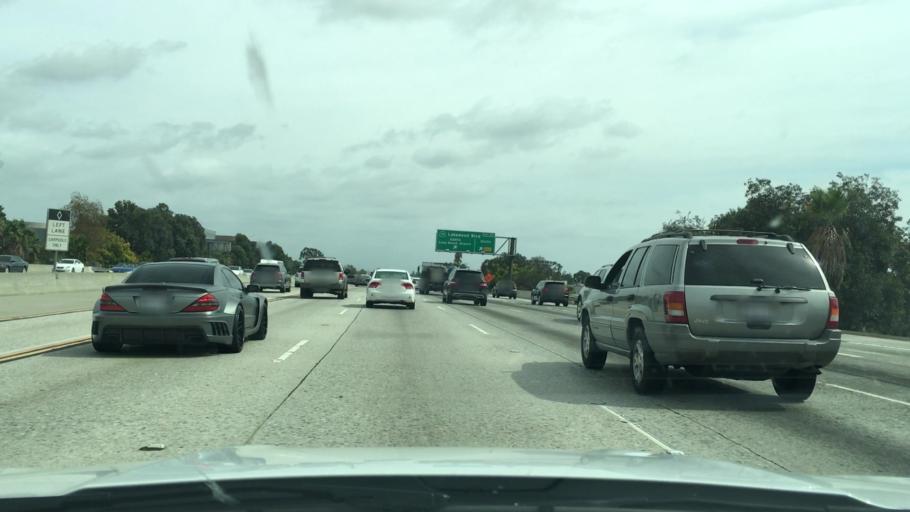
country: US
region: California
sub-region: Los Angeles County
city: Signal Hill
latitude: 33.8077
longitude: -118.1532
